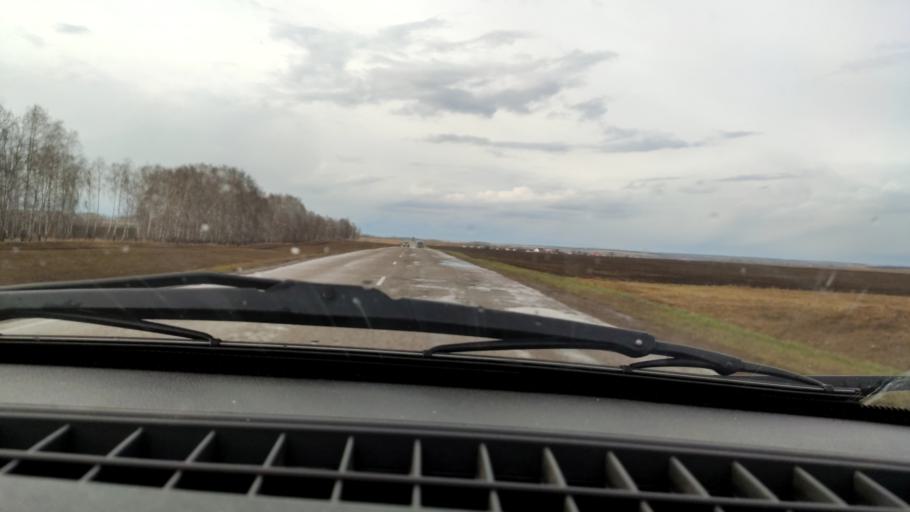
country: RU
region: Bashkortostan
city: Kushnarenkovo
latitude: 55.0841
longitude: 55.0650
